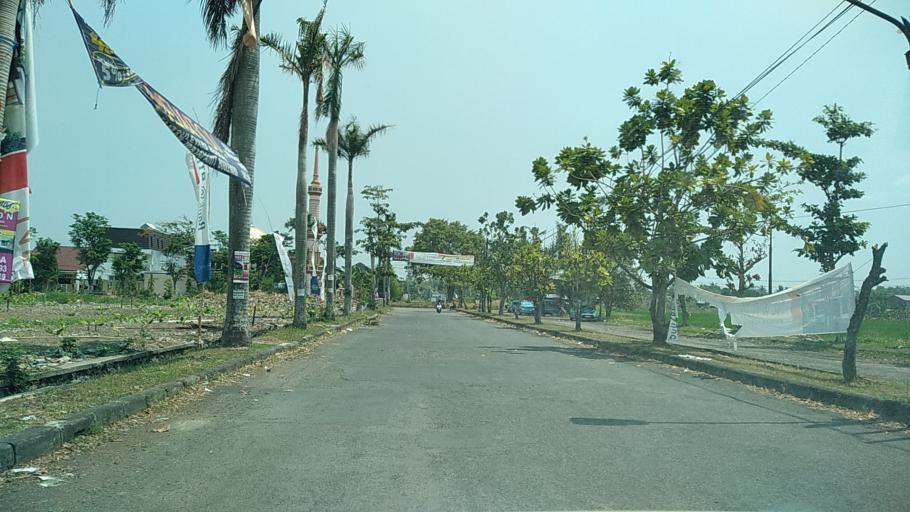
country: ID
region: Central Java
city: Mranggen
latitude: -7.0090
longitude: 110.4842
